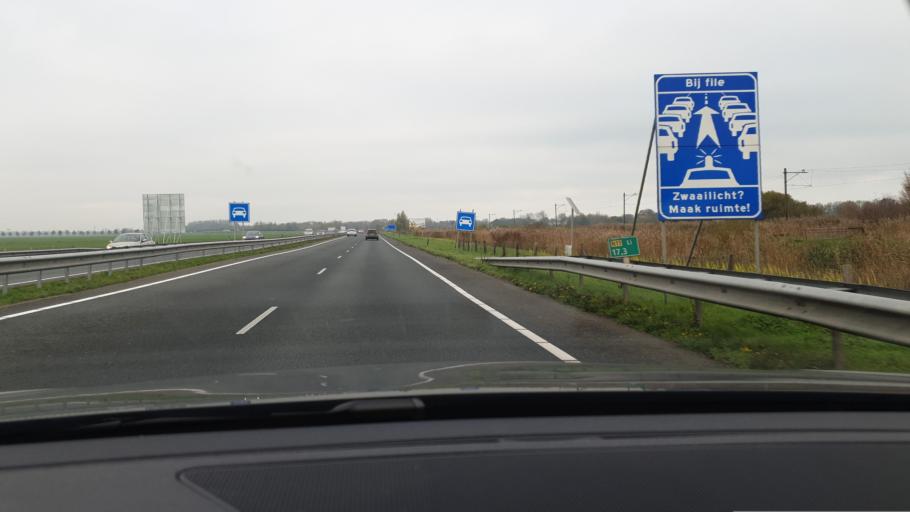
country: NL
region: South Holland
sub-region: Bodegraven-Reeuwijk
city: Bodegraven
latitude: 52.0944
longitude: 4.7322
